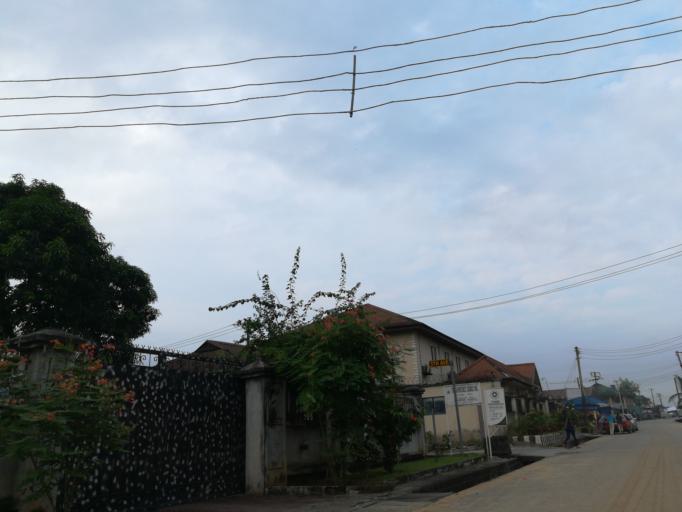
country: NG
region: Rivers
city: Port Harcourt
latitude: 4.8447
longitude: 7.0559
